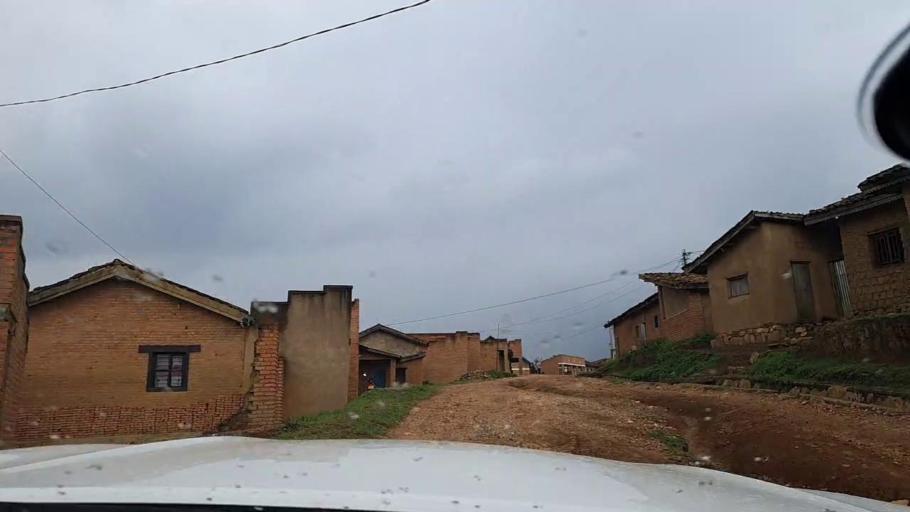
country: RW
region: Western Province
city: Kibuye
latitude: -2.1065
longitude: 29.4842
